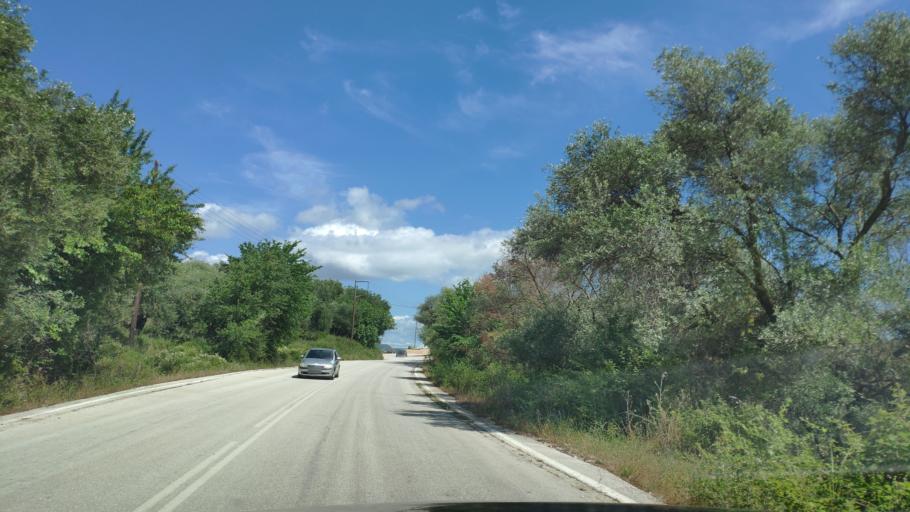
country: AL
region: Vlore
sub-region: Rrethi i Sarandes
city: Konispol
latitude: 39.6194
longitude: 20.2015
